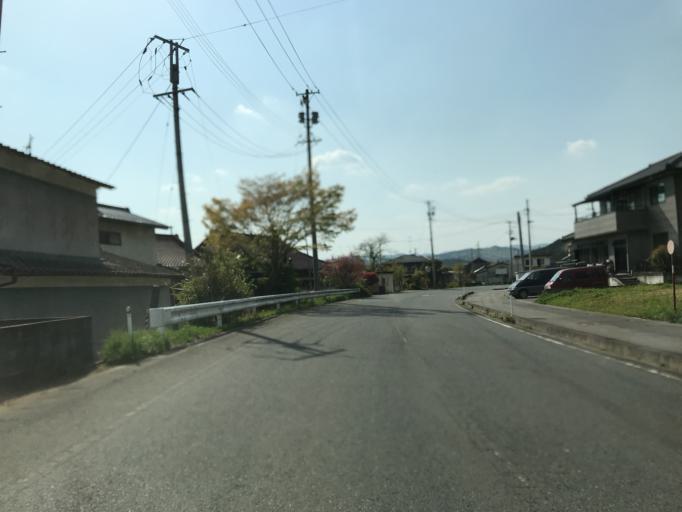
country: JP
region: Fukushima
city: Iwaki
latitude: 37.0055
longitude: 140.7587
